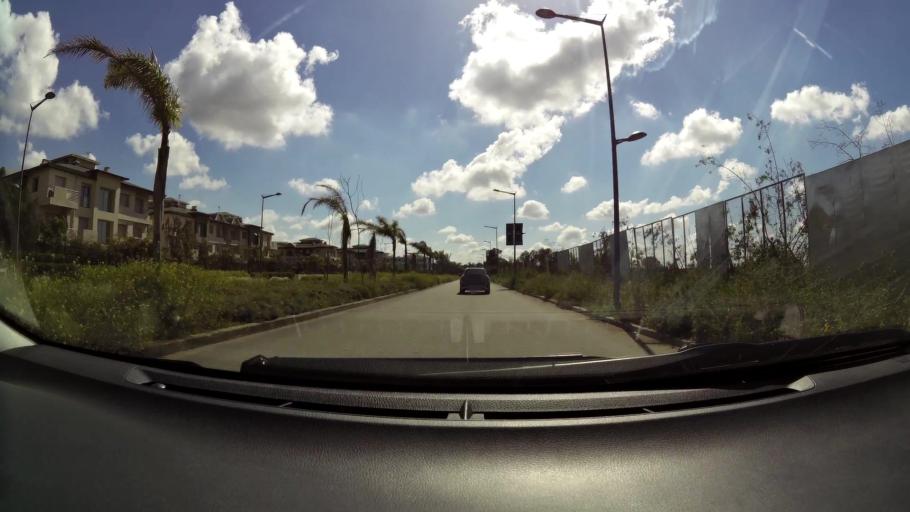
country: MA
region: Grand Casablanca
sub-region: Nouaceur
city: Bouskoura
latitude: 33.4739
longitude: -7.6103
